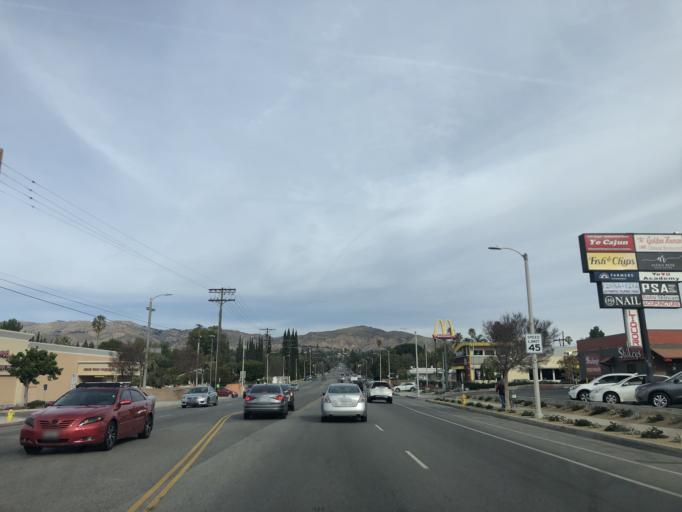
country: US
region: California
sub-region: Los Angeles County
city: Northridge
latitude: 34.2579
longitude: -118.5361
